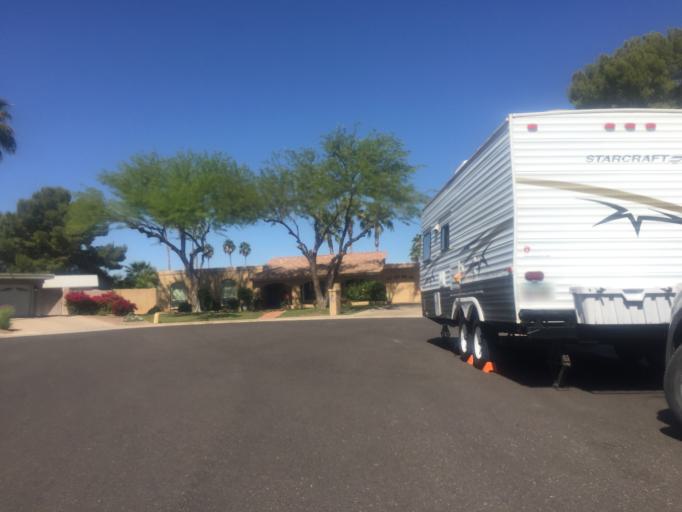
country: US
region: Arizona
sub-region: Maricopa County
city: Paradise Valley
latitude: 33.5716
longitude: -112.0117
